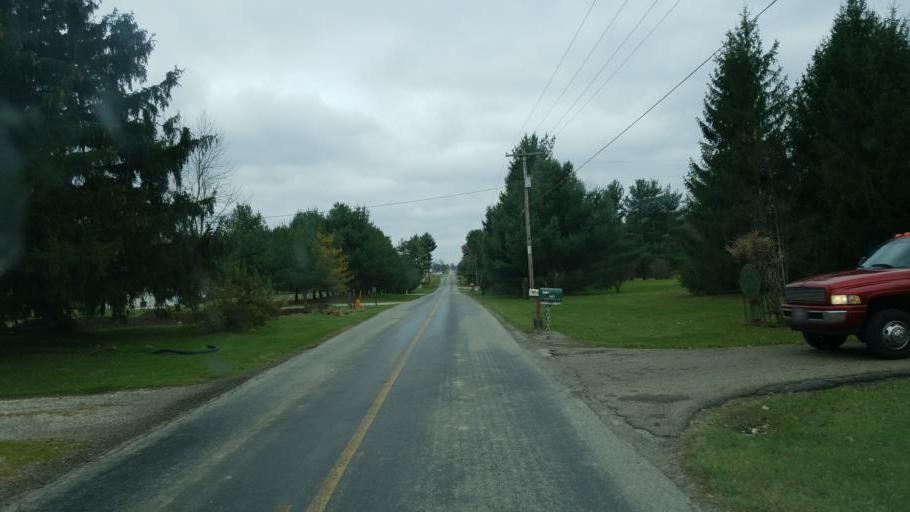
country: US
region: Ohio
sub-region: Licking County
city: Johnstown
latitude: 40.2013
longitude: -82.7564
